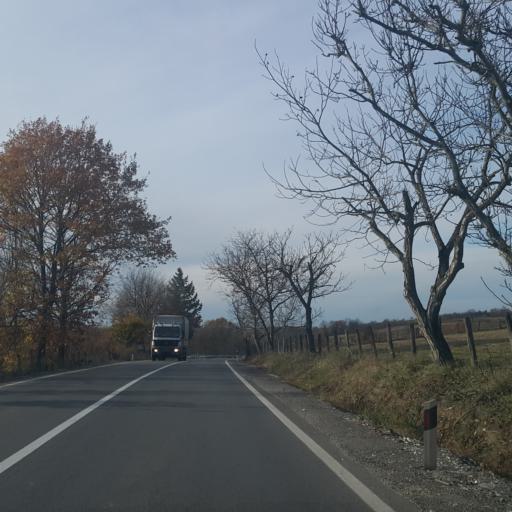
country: RS
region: Central Serbia
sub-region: Sumadijski Okrug
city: Arangelovac
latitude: 44.3400
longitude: 20.4200
